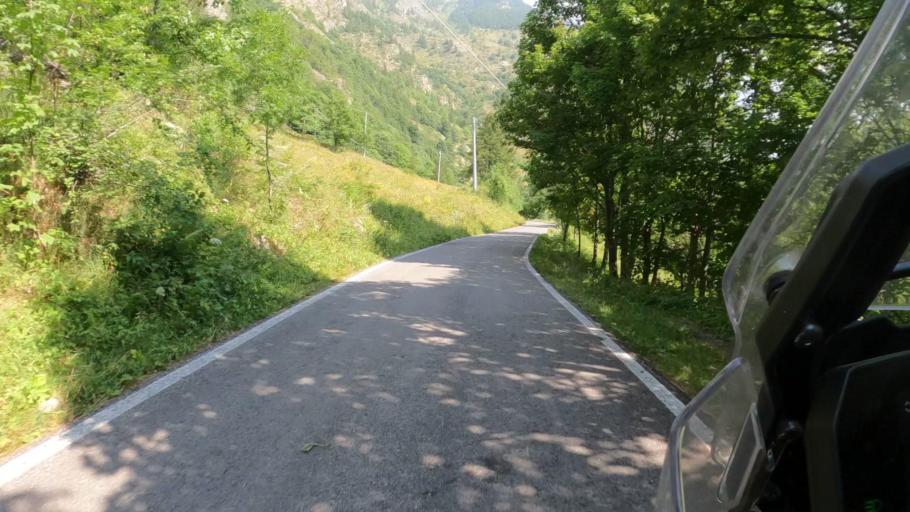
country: IT
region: Piedmont
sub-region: Provincia di Cuneo
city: Canosio
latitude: 44.4367
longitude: 7.0571
